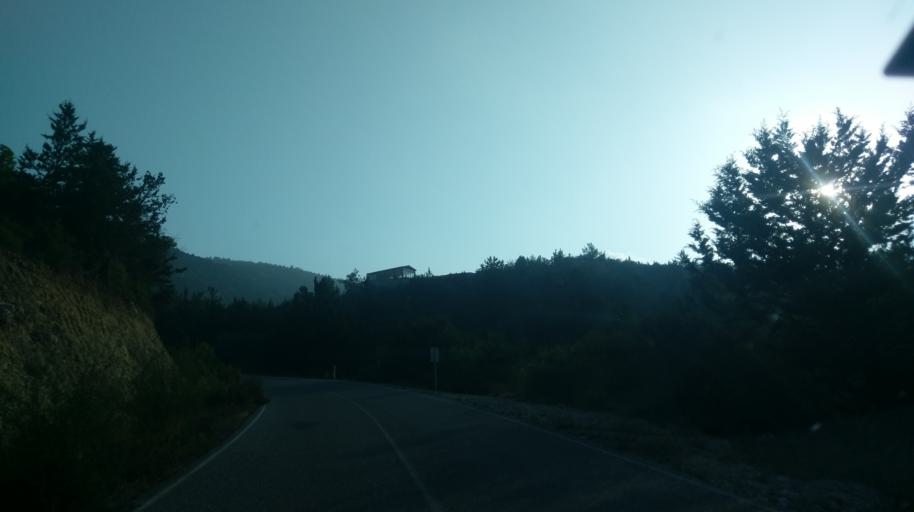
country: CY
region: Ammochostos
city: Trikomo
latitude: 35.4057
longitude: 33.9043
